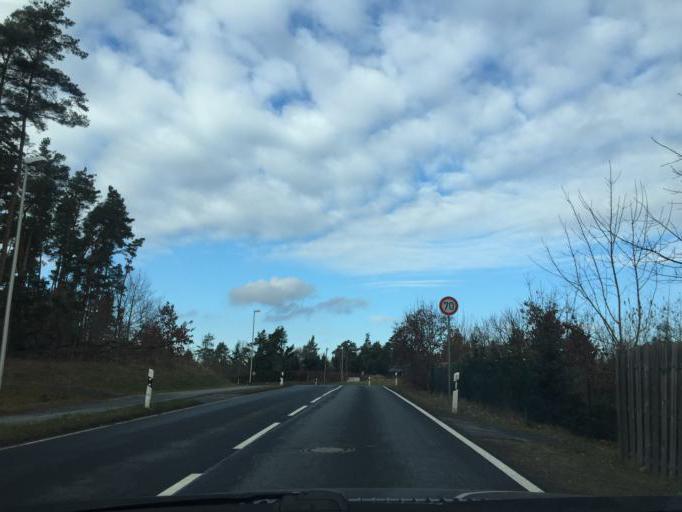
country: DE
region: Saxony
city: Ottendorf-Okrilla
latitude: 51.1869
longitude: 13.7823
